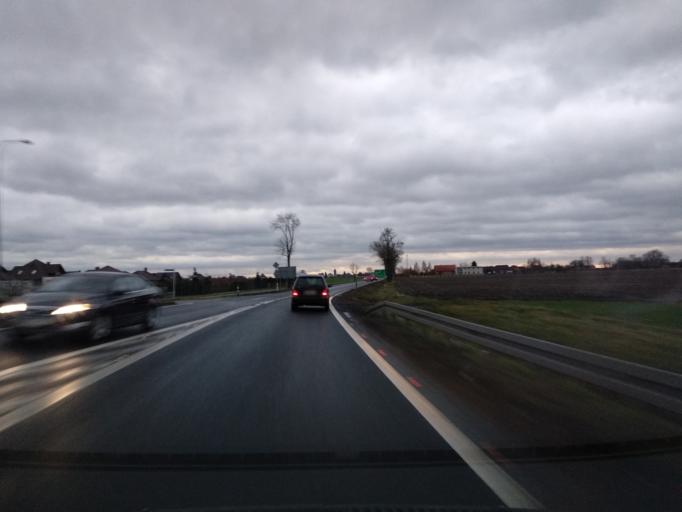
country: PL
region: Greater Poland Voivodeship
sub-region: Powiat koninski
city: Rychwal
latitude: 52.0658
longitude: 18.1639
